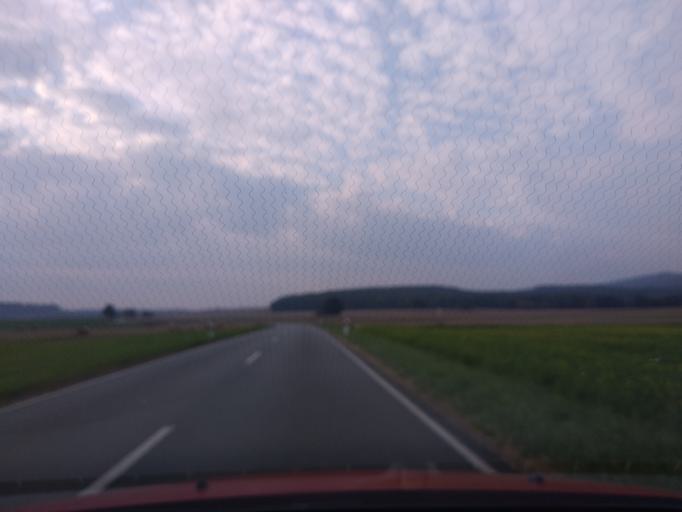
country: DE
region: Hesse
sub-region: Regierungsbezirk Kassel
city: Zierenberg
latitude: 51.4278
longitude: 9.3330
